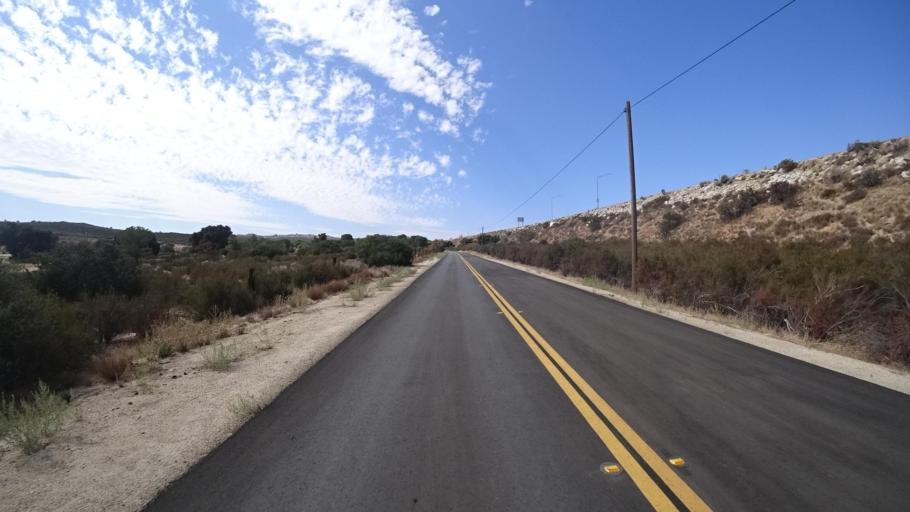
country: US
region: California
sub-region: San Diego County
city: Campo
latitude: 32.6780
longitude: -116.2946
